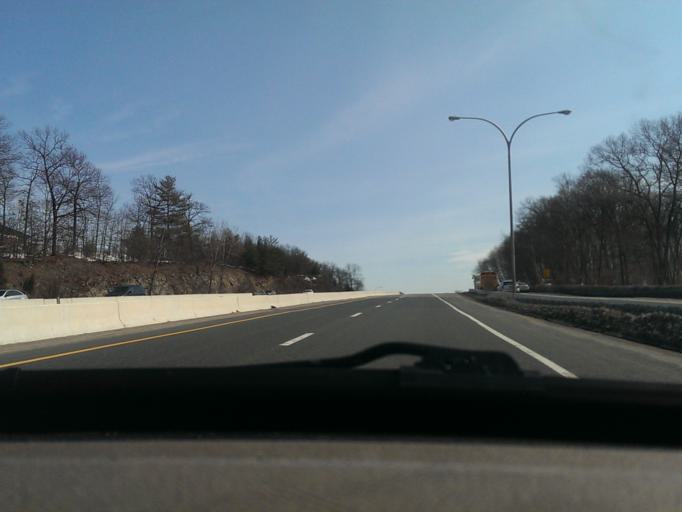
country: US
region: Rhode Island
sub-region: Providence County
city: Cumberland Hill
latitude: 41.9388
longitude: -71.4710
